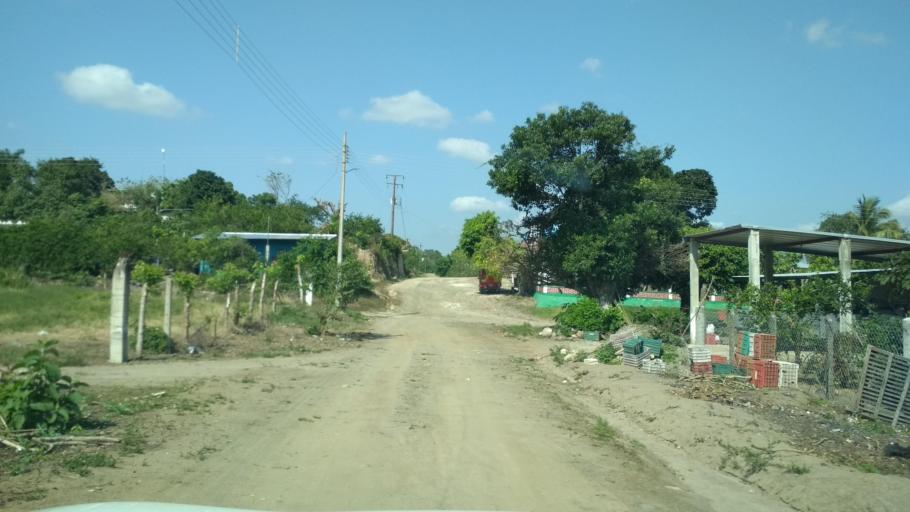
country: MX
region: Puebla
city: San Jose Acateno
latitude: 20.1888
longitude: -97.1559
